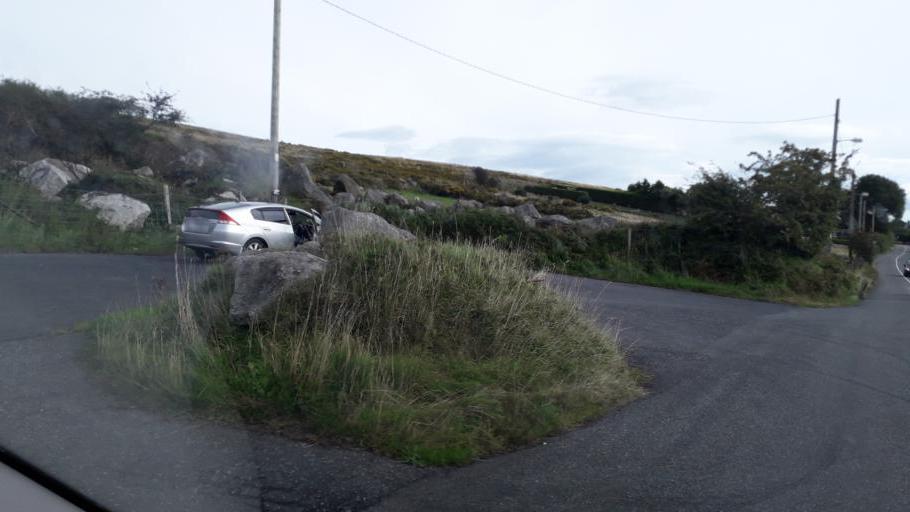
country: IE
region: Leinster
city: Ballinteer
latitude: 53.2254
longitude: -6.2452
